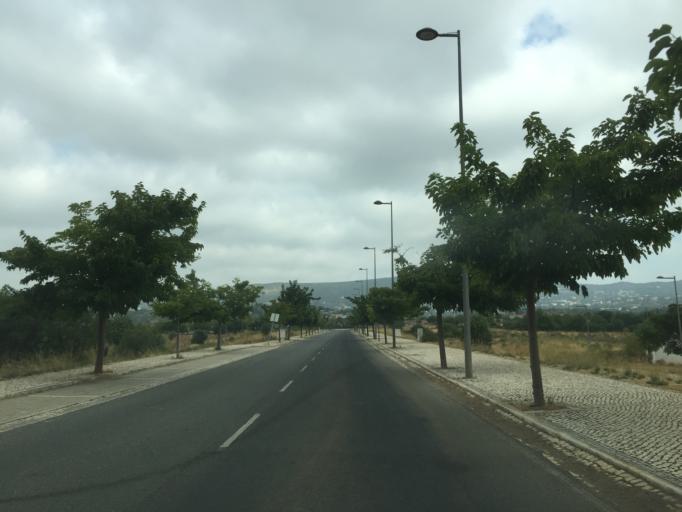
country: PT
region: Faro
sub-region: Faro
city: Santa Barbara de Nexe
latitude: 37.0836
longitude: -7.9782
